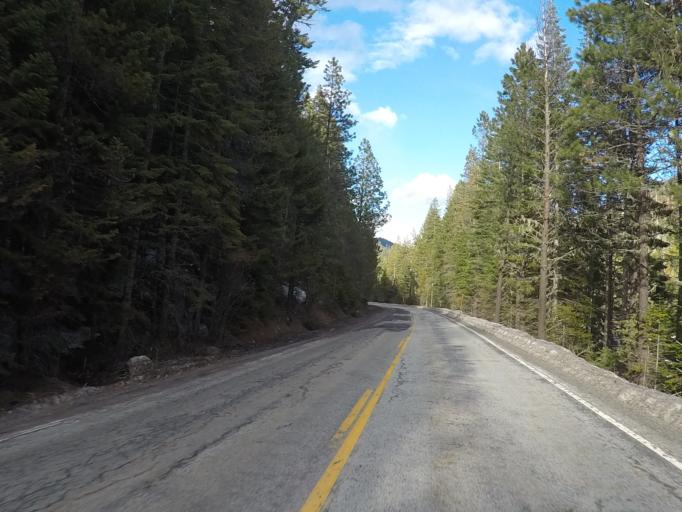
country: US
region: Montana
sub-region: Mineral County
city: Superior
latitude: 46.4936
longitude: -114.8672
